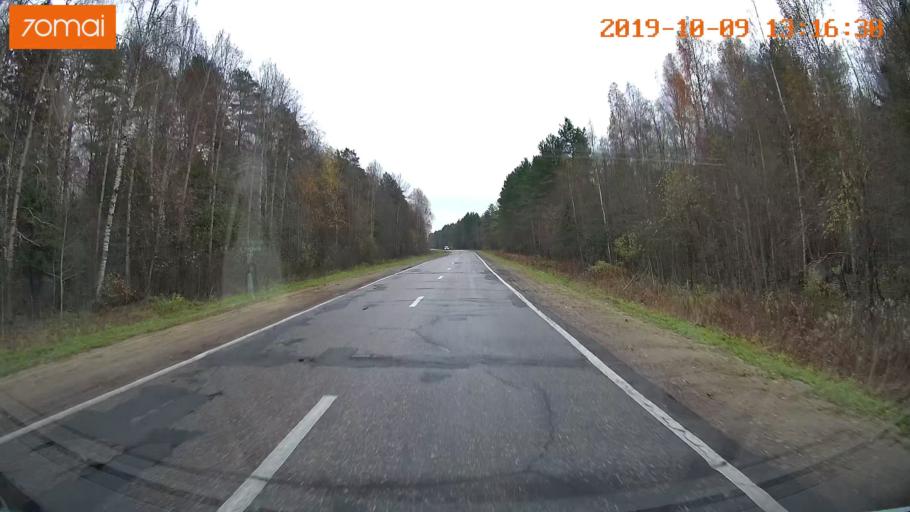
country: RU
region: Jaroslavl
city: Lyubim
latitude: 58.3608
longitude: 40.7668
